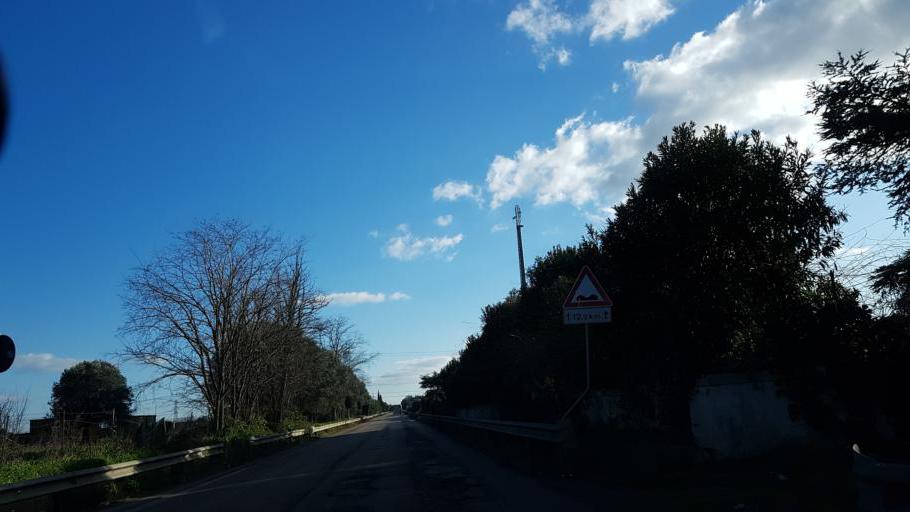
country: IT
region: Apulia
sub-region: Provincia di Brindisi
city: La Rosa
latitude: 40.6090
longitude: 17.9540
